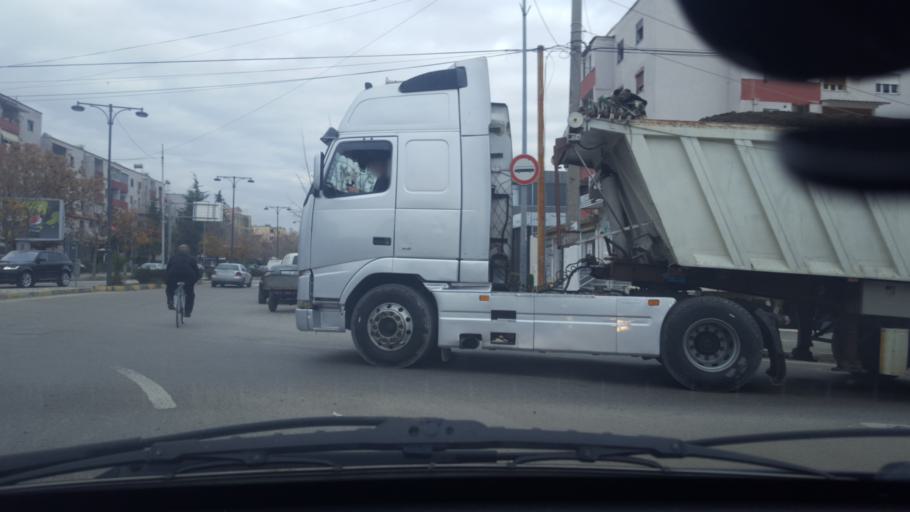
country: AL
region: Elbasan
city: Elbasan
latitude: 41.1082
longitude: 20.0713
